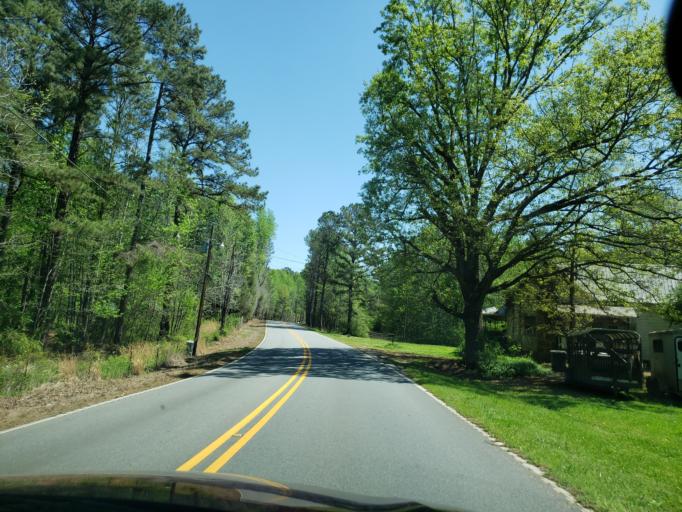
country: US
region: Alabama
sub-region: Tallapoosa County
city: Camp Hill
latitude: 32.6971
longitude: -85.7273
